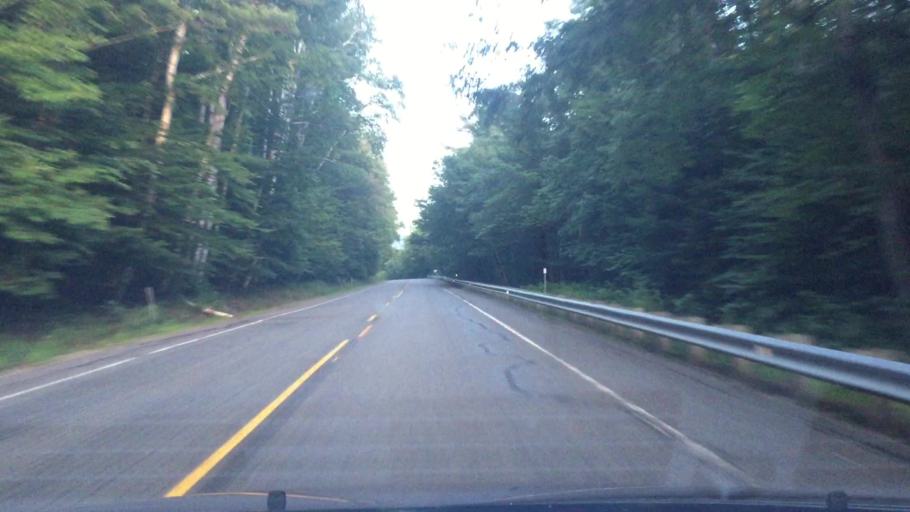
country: US
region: New Hampshire
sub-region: Grafton County
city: Woodstock
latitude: 44.0489
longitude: -71.5635
